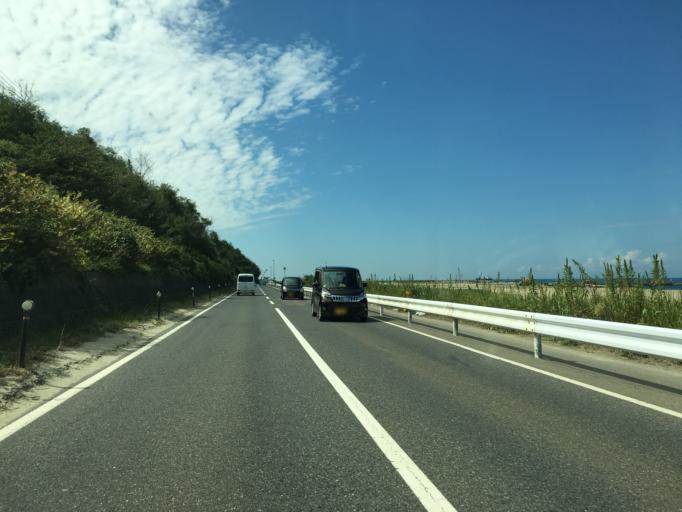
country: JP
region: Niigata
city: Niigata-shi
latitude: 37.9358
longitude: 139.0467
